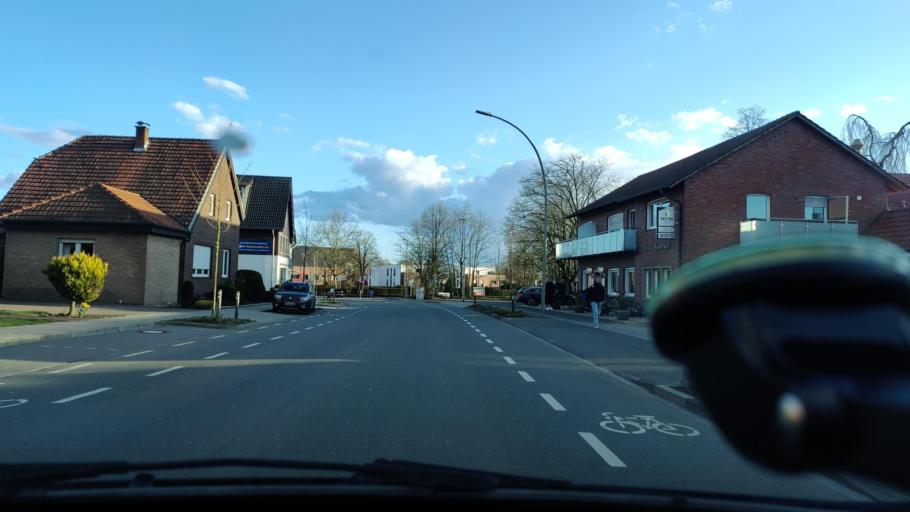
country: DE
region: North Rhine-Westphalia
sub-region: Regierungsbezirk Munster
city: Coesfeld
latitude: 51.8999
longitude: 7.1884
